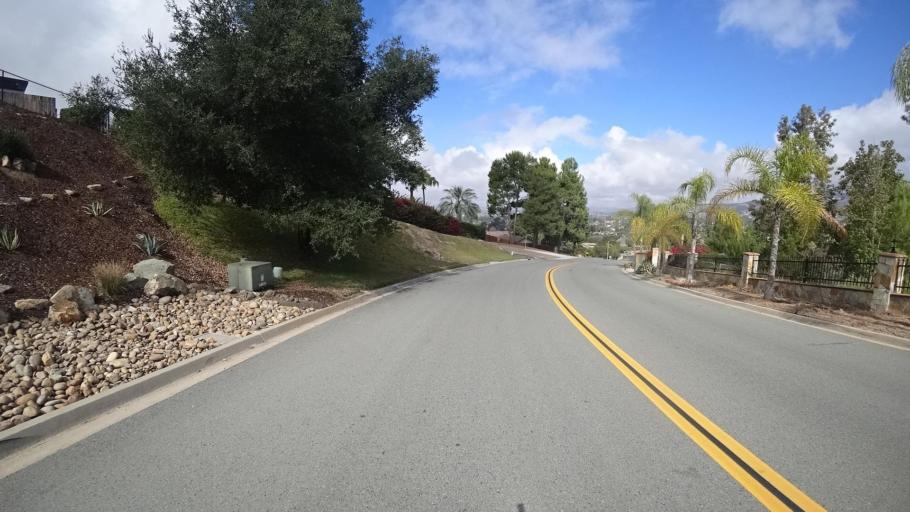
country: US
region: California
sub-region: San Diego County
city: Granite Hills
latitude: 32.7784
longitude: -116.9025
